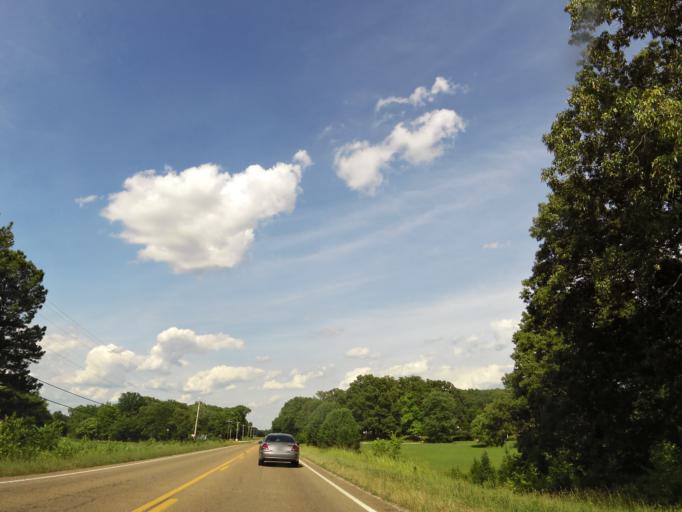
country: US
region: Tennessee
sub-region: Carroll County
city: Bruceton
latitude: 36.0349
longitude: -88.3231
